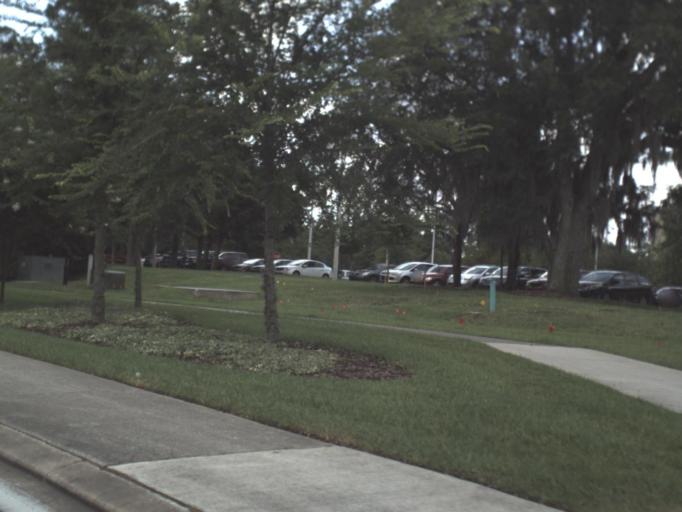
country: US
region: Florida
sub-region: Alachua County
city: Gainesville
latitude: 29.6397
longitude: -82.3417
